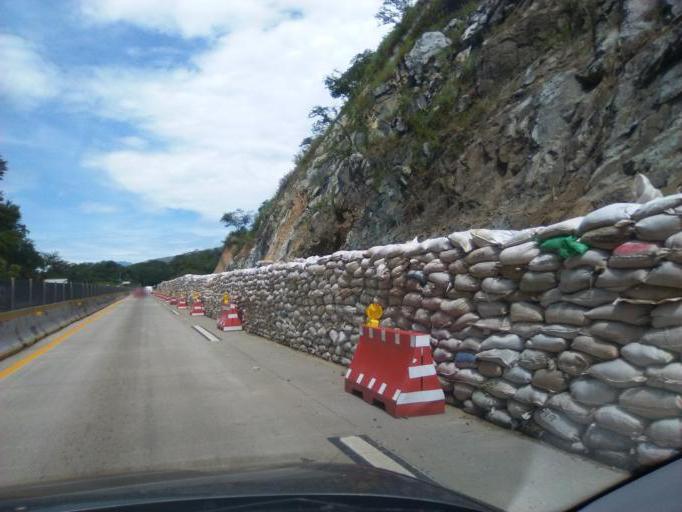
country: MX
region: Guerrero
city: Tierra Colorada
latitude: 17.1793
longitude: -99.5523
